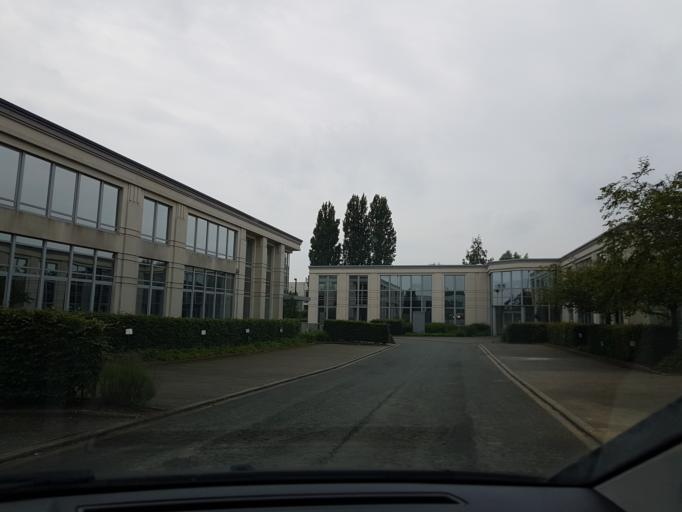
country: BE
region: Flanders
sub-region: Provincie Vlaams-Brabant
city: Zaventem
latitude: 50.8759
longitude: 4.4901
